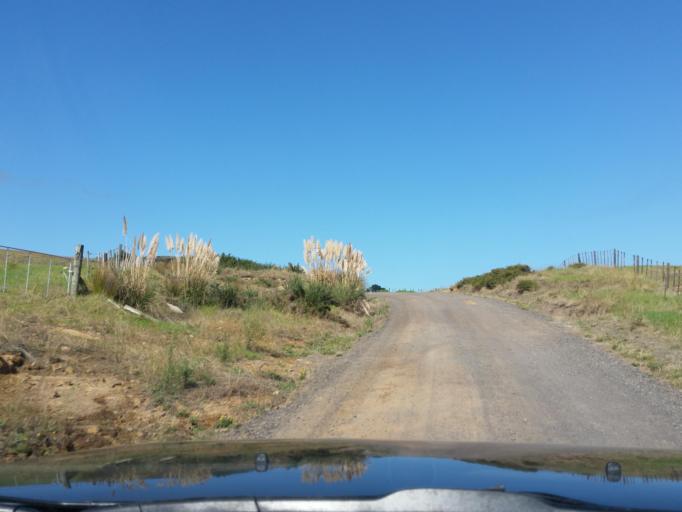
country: NZ
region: Northland
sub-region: Kaipara District
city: Dargaville
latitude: -35.7103
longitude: 173.5395
